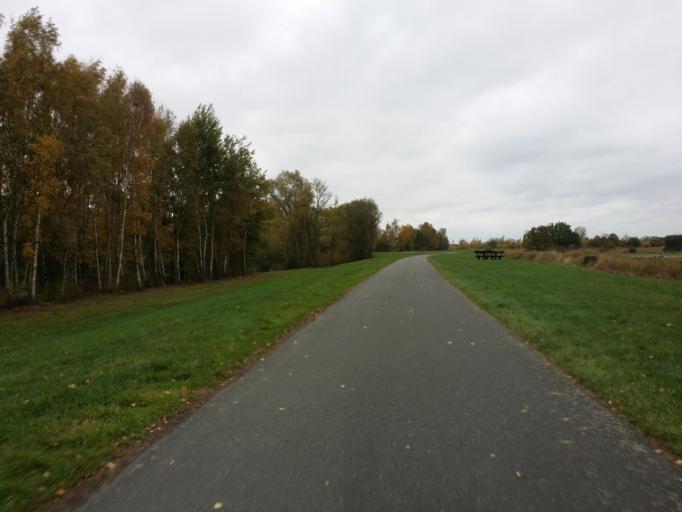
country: DE
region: Lower Saxony
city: Stuhr
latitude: 53.0518
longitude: 8.7566
